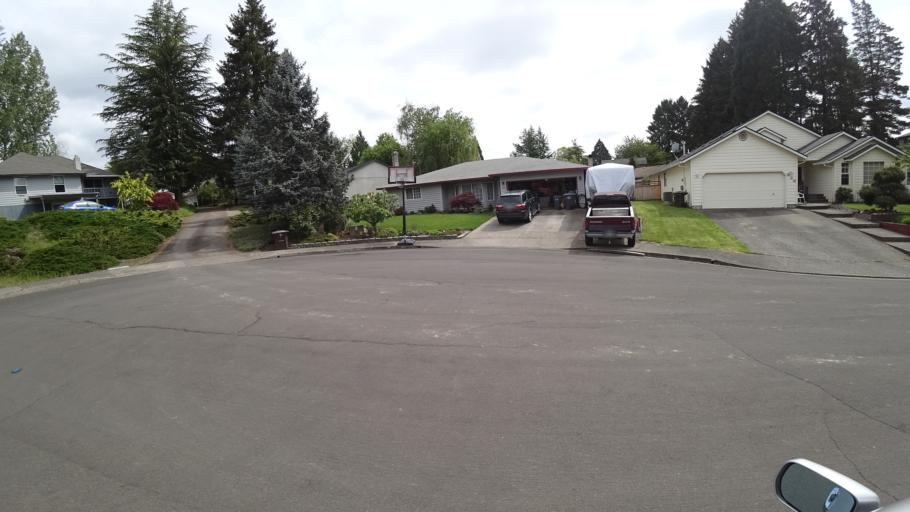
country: US
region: Oregon
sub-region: Washington County
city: Hillsboro
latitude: 45.5261
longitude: -123.0005
